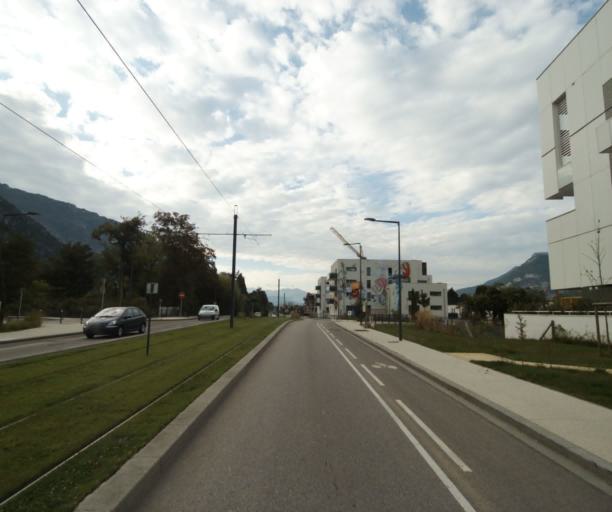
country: FR
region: Rhone-Alpes
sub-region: Departement de l'Isere
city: Fontanil-Cornillon
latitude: 45.2538
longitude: 5.6623
